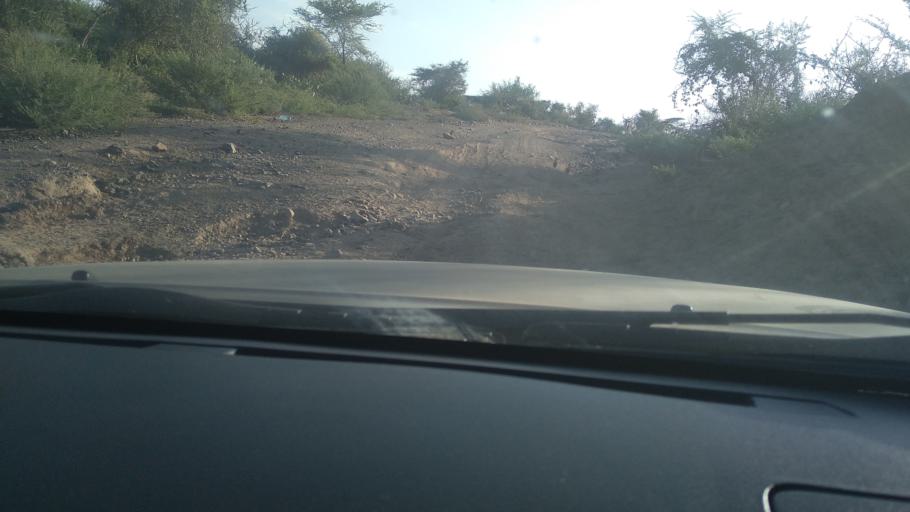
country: ET
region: Oromiya
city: Hirna
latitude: 9.3781
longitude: 40.9305
